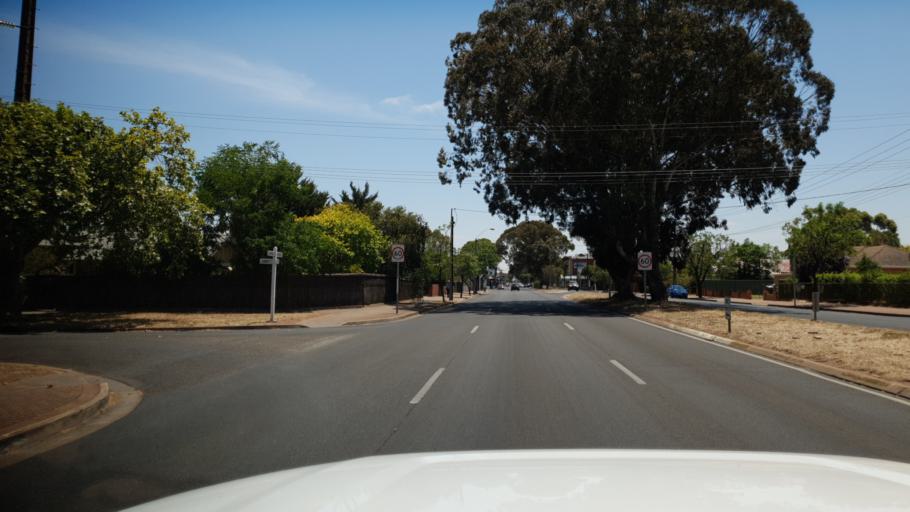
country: AU
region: South Australia
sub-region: Mitcham
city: Clapham
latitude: -34.9840
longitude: 138.5921
